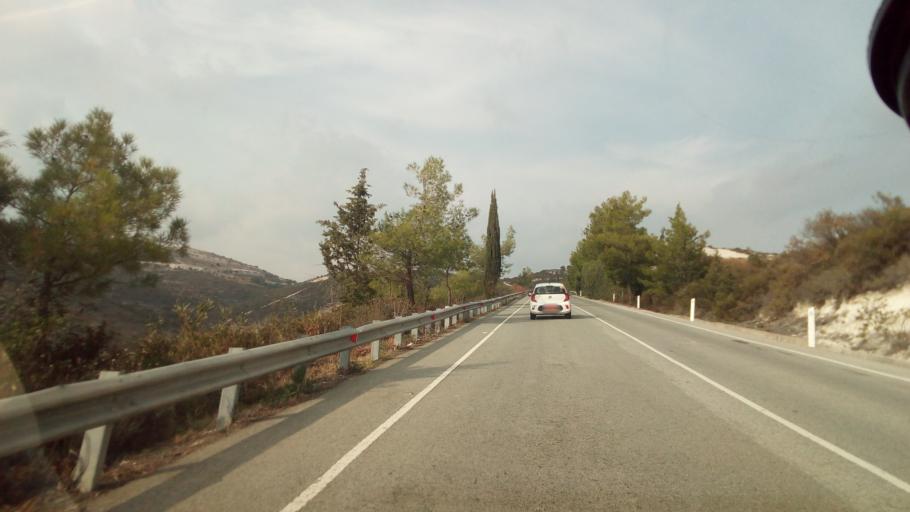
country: CY
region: Larnaka
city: Kofinou
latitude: 34.8461
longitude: 33.3283
